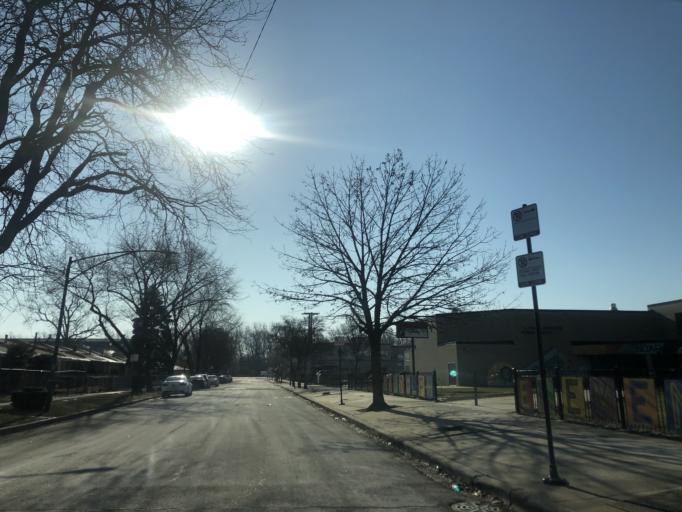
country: US
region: Illinois
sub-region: Cook County
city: Evergreen Park
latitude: 41.7612
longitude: -87.6759
